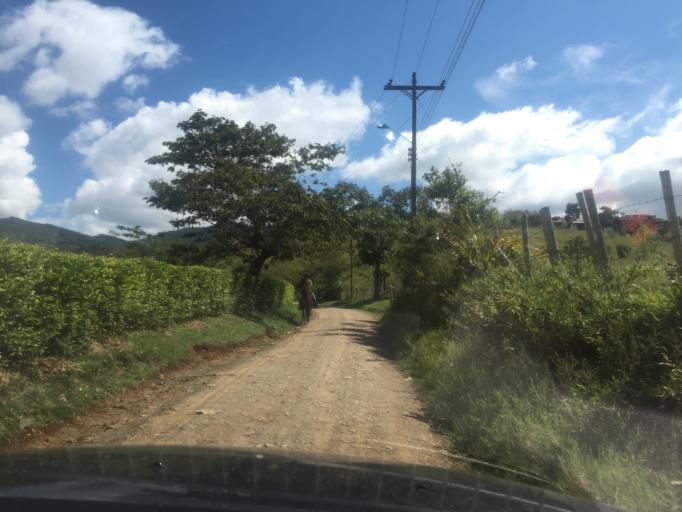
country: CO
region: Valle del Cauca
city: Yumbo
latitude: 3.6618
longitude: -76.5599
